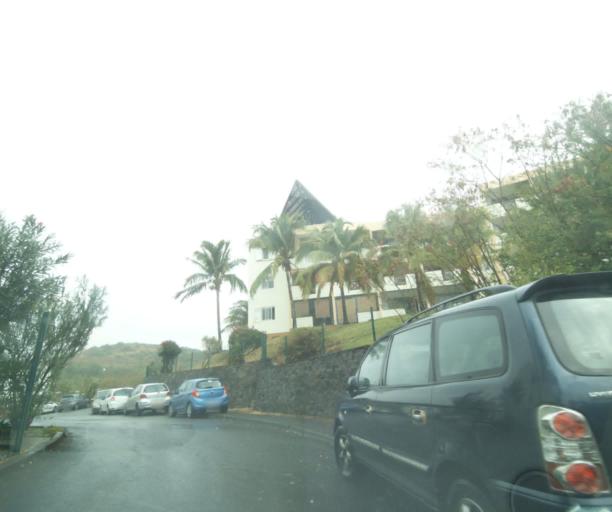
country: RE
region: Reunion
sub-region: Reunion
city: Saint-Paul
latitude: -21.0318
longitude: 55.2288
